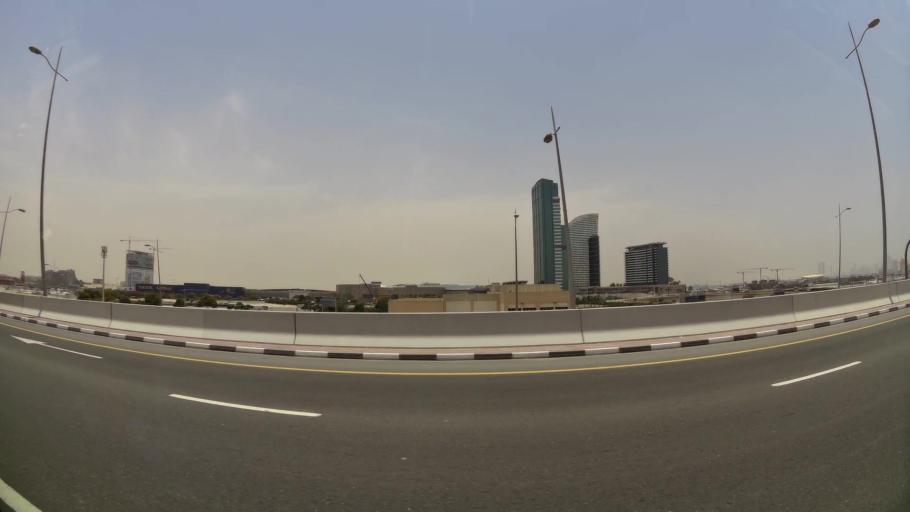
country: AE
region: Ash Shariqah
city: Sharjah
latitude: 25.2287
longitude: 55.3524
